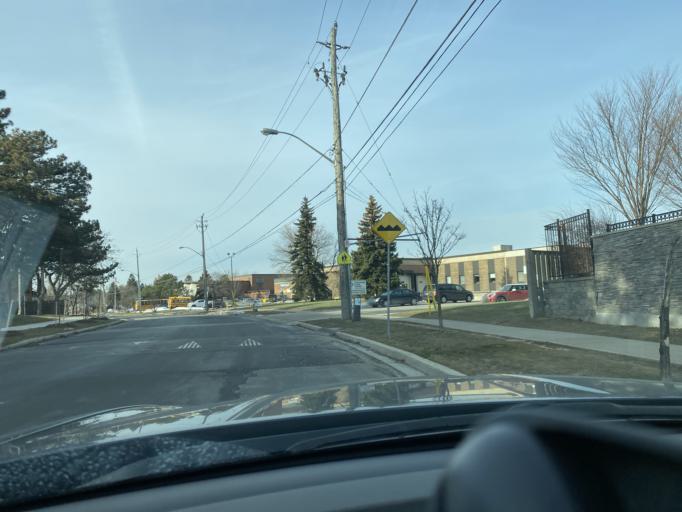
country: CA
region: Ontario
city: Scarborough
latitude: 43.7161
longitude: -79.2844
